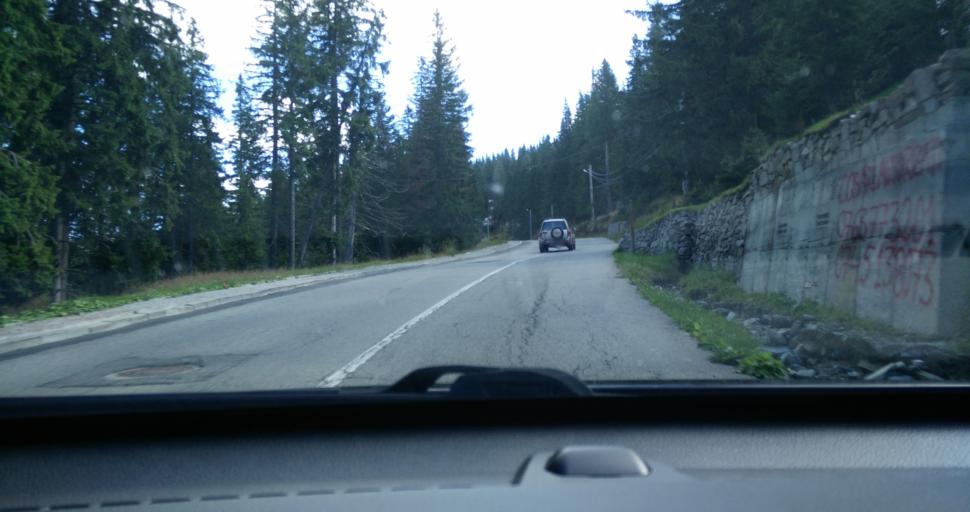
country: RO
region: Gorj
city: Novaci-Straini
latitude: 45.2826
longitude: 23.6894
